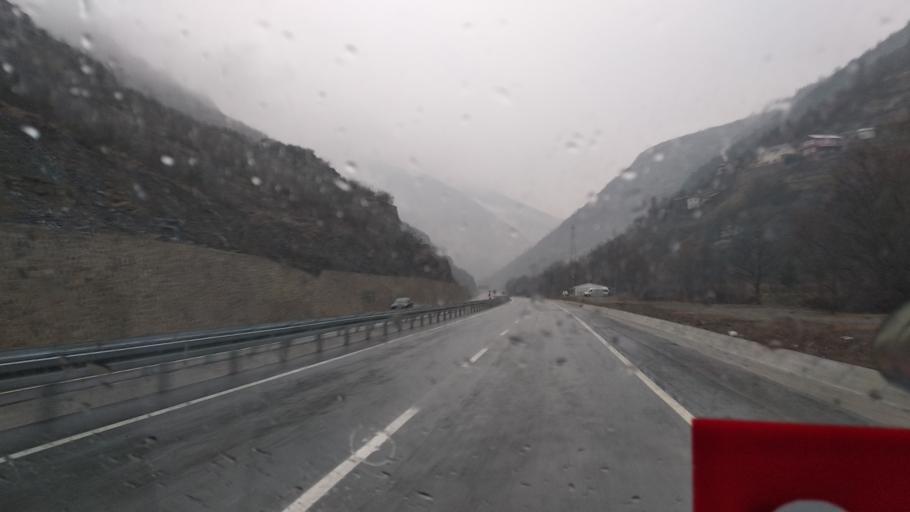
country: TR
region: Trabzon
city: Macka
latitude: 40.7878
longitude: 39.5786
